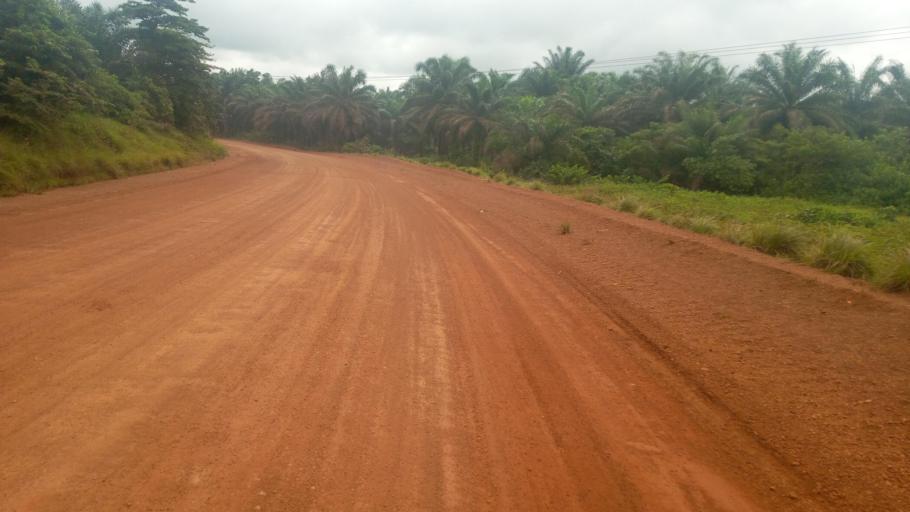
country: SL
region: Southern Province
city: Mogbwemo
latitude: 7.7262
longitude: -12.2778
